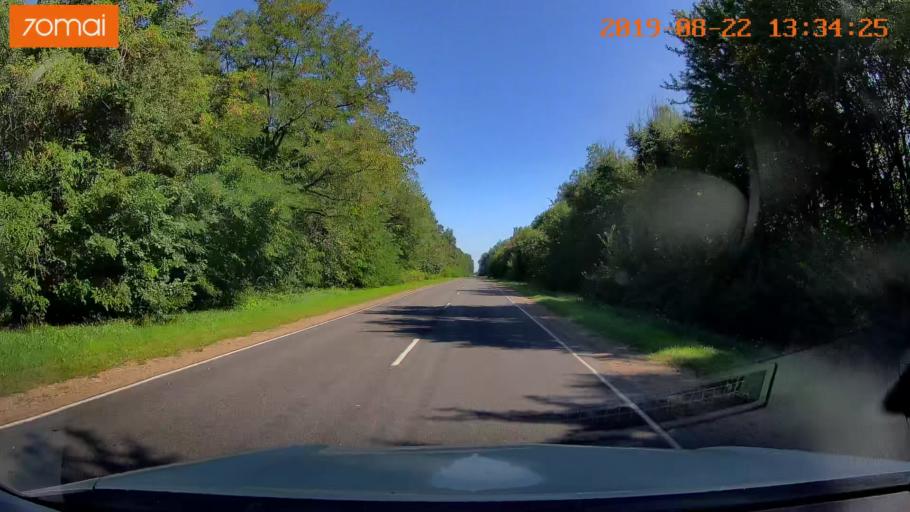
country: BY
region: Minsk
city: Staryya Darohi
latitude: 53.2153
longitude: 28.2409
